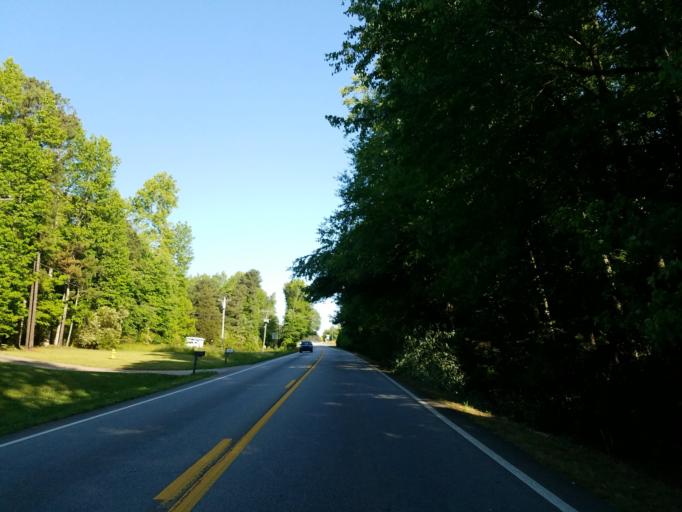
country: US
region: Georgia
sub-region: Carroll County
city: Villa Rica
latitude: 33.7571
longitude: -84.9395
